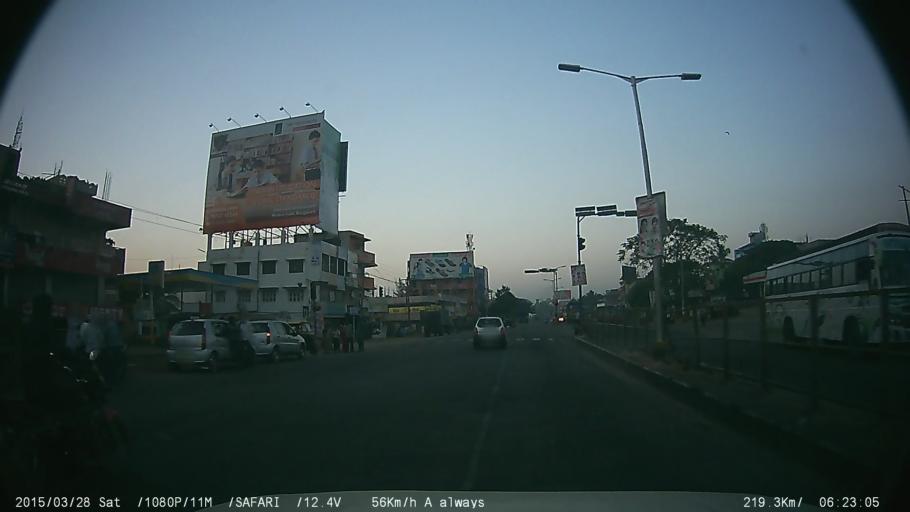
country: IN
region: Karnataka
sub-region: Ramanagara
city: Ramanagaram
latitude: 12.7233
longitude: 77.2753
